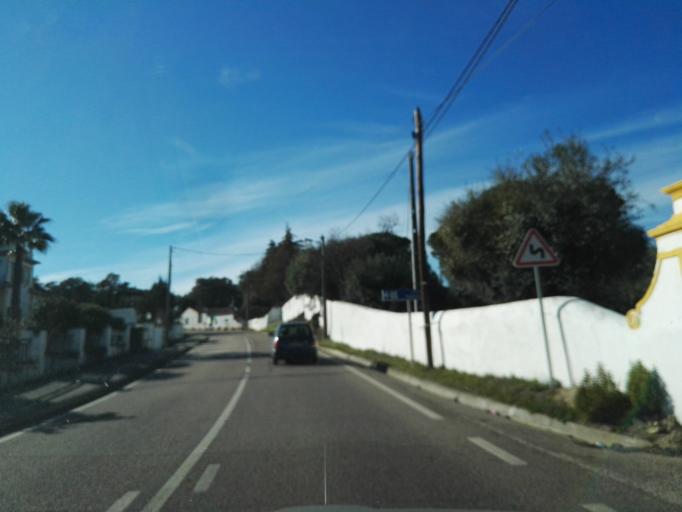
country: PT
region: Santarem
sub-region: Macao
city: Macao
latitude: 39.4665
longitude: -8.0492
